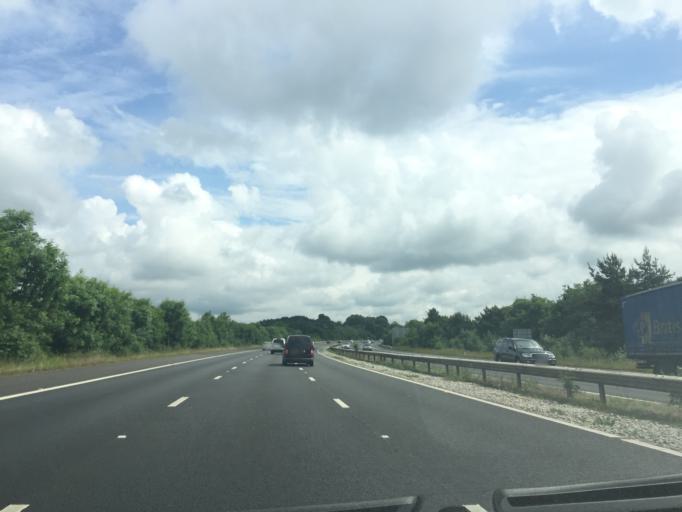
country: GB
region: England
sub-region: Hampshire
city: Cadnam
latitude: 50.9273
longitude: -1.5766
